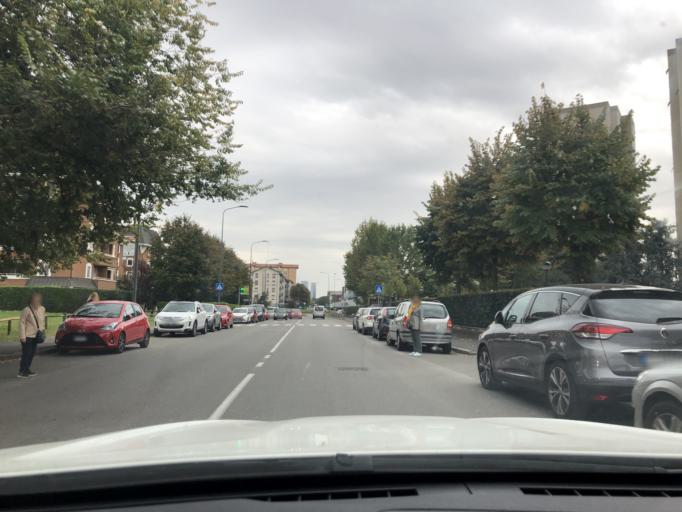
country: IT
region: Lombardy
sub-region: Citta metropolitana di Milano
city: Pero
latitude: 45.4990
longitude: 9.1101
